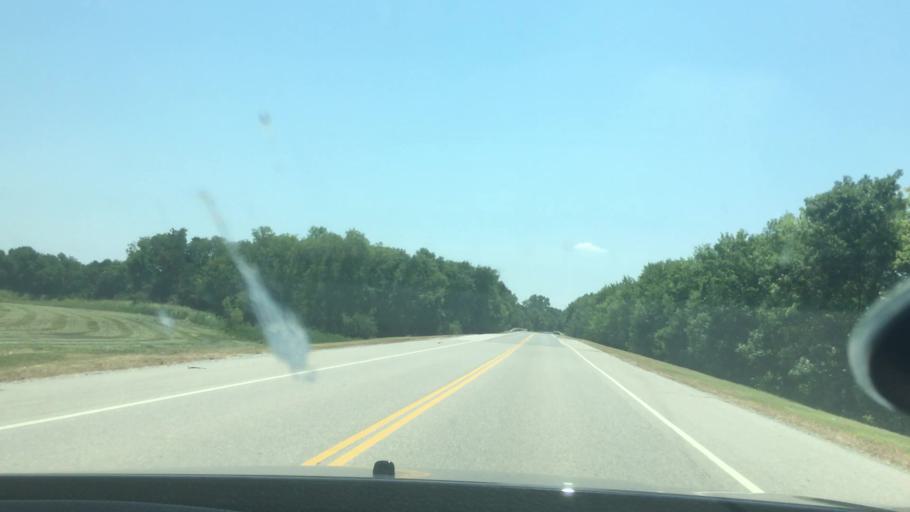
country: US
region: Oklahoma
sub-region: Coal County
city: Coalgate
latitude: 34.5391
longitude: -96.4083
